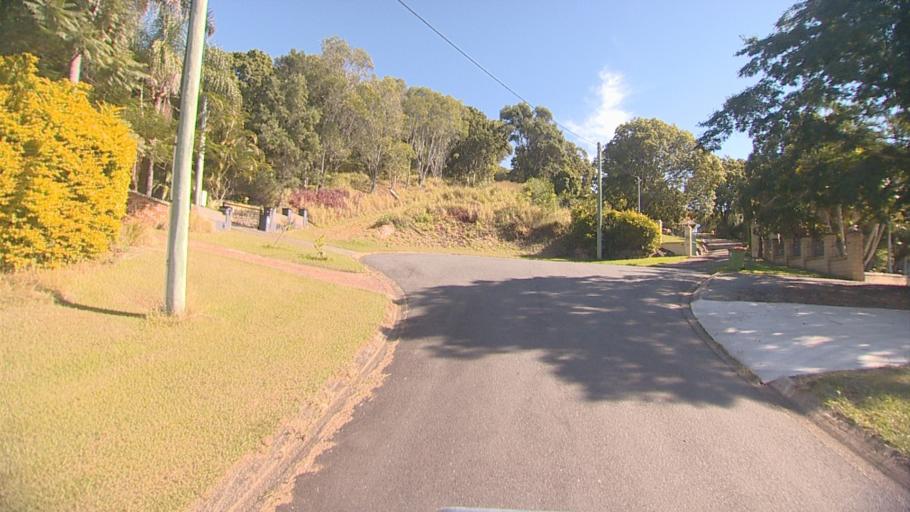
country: AU
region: Queensland
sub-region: Logan
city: Windaroo
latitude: -27.7434
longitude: 153.1797
